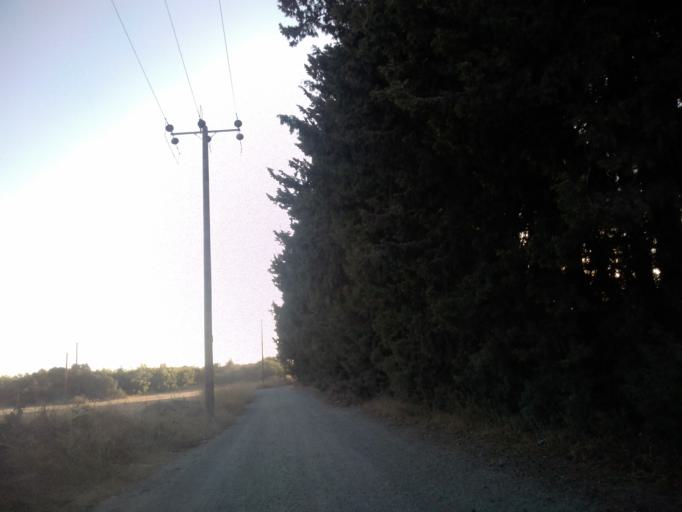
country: CY
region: Limassol
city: Ypsonas
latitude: 34.6707
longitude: 32.9713
